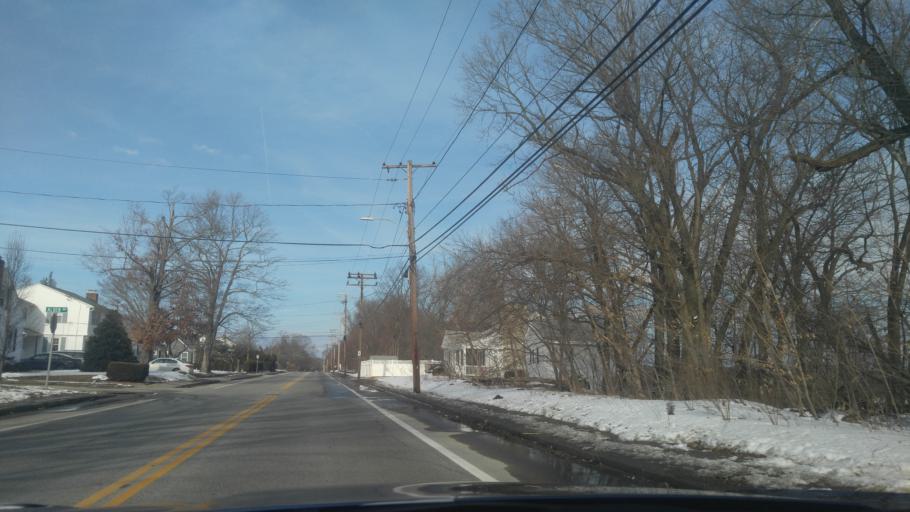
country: US
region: Rhode Island
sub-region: Kent County
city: West Warwick
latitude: 41.7272
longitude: -71.4902
